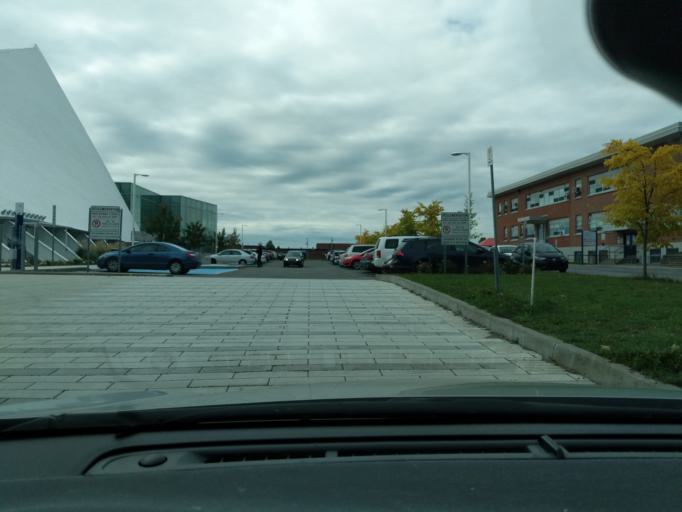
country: CA
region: Quebec
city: L'Ancienne-Lorette
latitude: 46.7707
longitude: -71.2940
